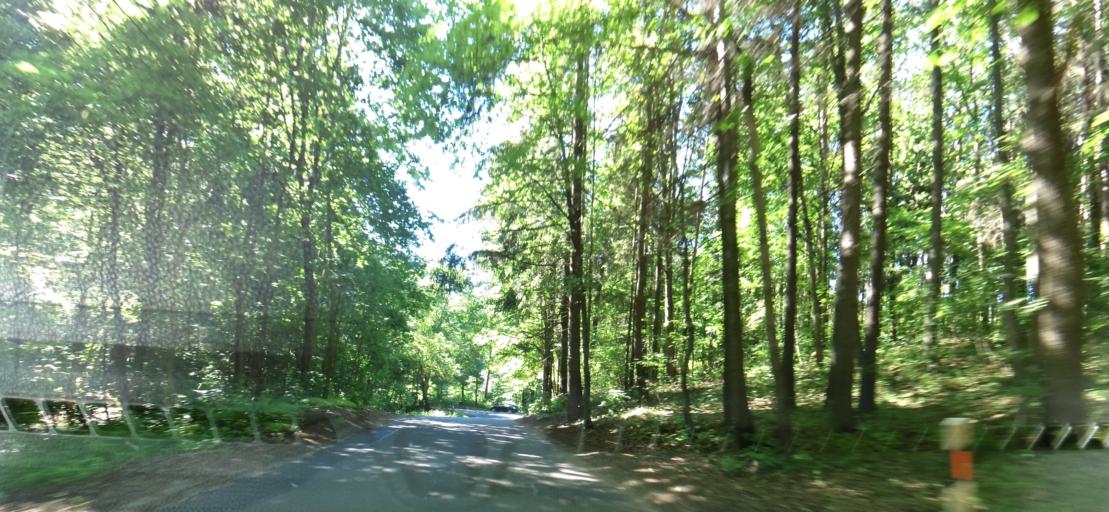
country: LT
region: Vilnius County
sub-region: Vilnius
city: Fabijoniskes
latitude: 54.7493
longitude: 25.3000
